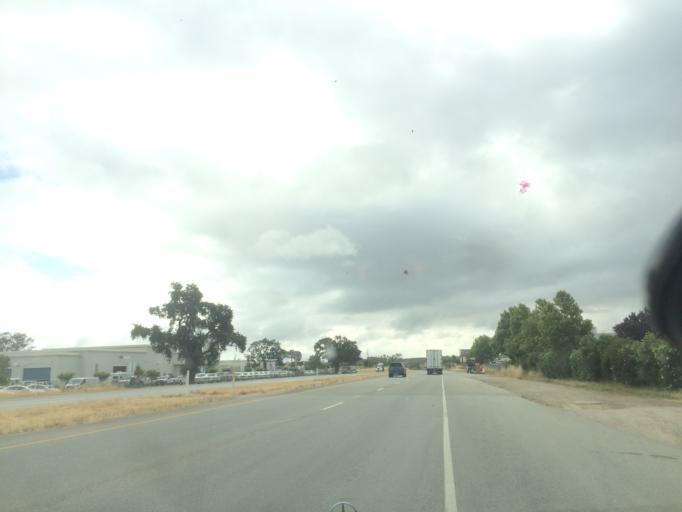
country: US
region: California
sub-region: San Luis Obispo County
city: Paso Robles
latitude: 35.6444
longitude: -120.6579
